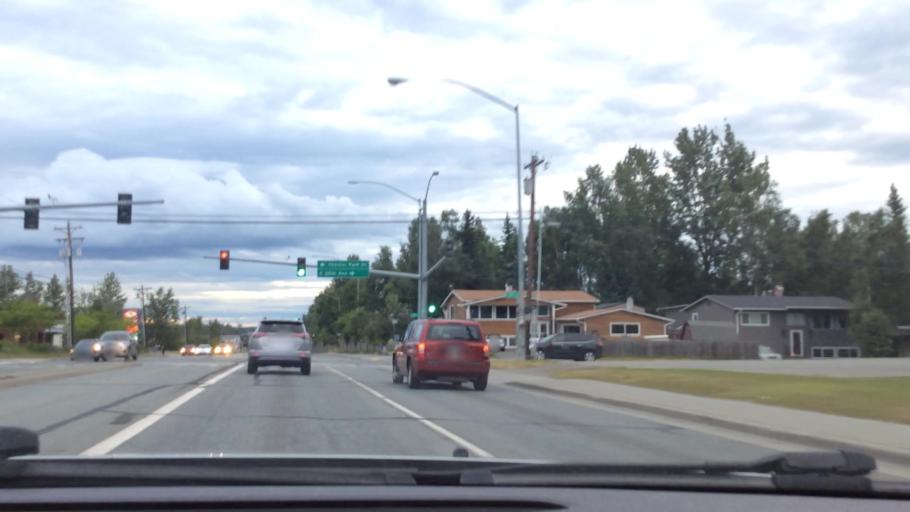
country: US
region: Alaska
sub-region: Anchorage Municipality
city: Elmendorf Air Force Base
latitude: 61.2022
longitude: -149.7333
